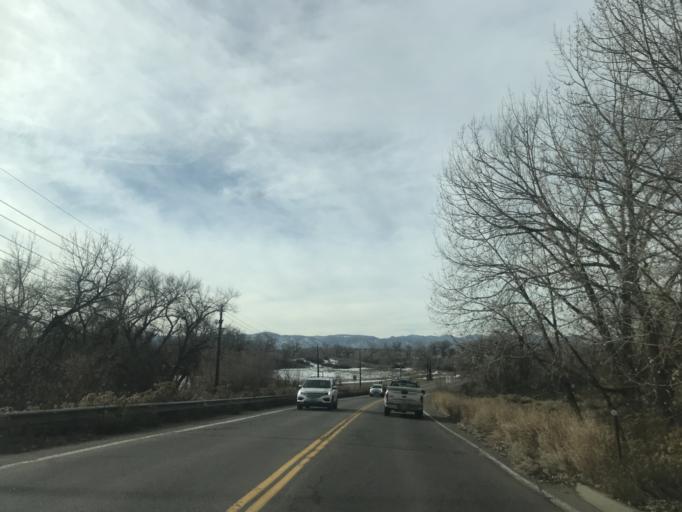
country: US
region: Colorado
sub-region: Douglas County
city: Highlands Ranch
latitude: 39.5647
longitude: -104.9992
